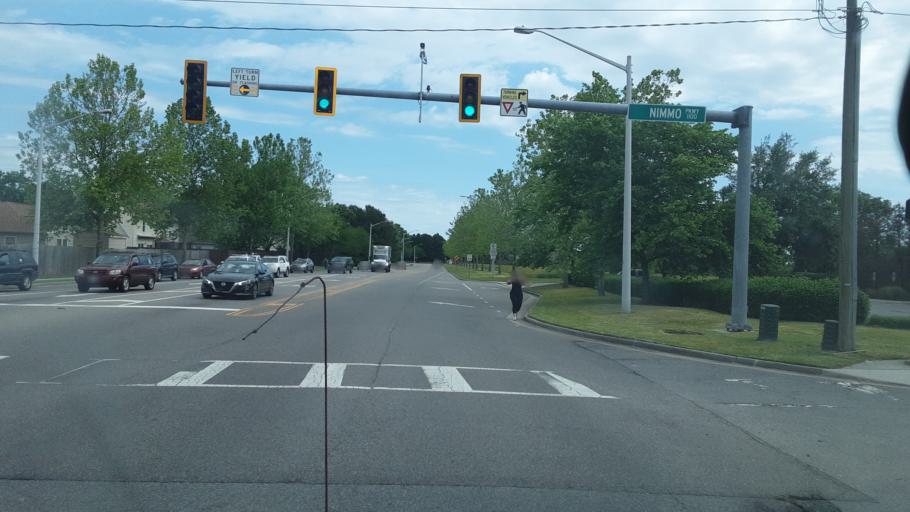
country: US
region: Virginia
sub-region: City of Virginia Beach
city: Virginia Beach
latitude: 36.7609
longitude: -76.0050
